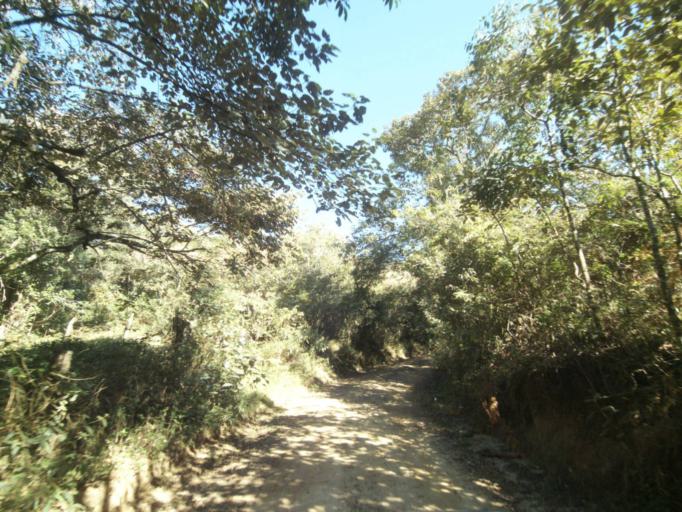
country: BR
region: Parana
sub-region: Tibagi
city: Tibagi
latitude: -24.5457
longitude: -50.4682
